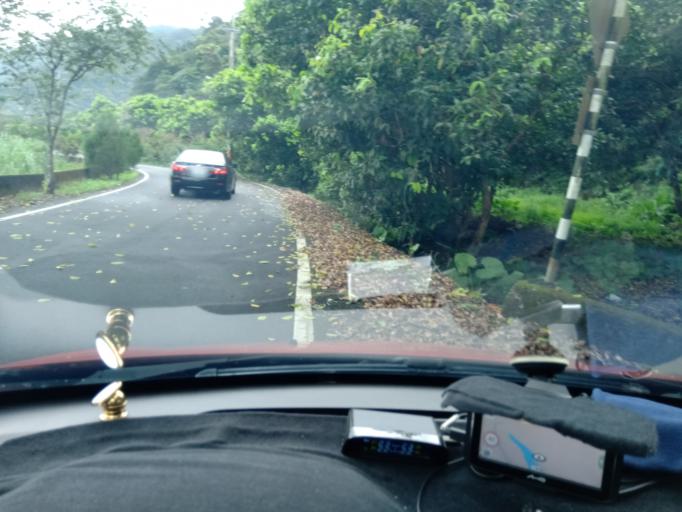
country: TW
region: Taiwan
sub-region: Yilan
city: Yilan
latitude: 24.7828
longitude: 121.7042
